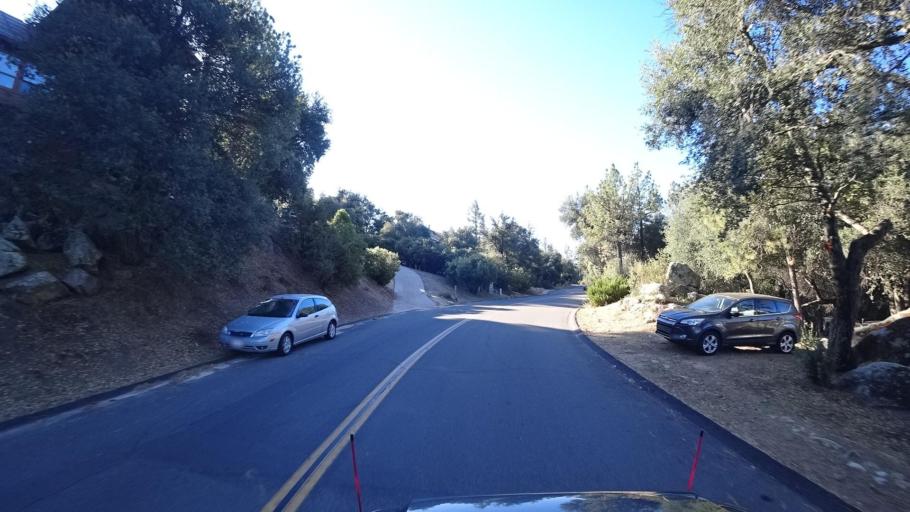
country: US
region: California
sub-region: San Diego County
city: Pine Valley
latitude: 32.8428
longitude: -116.5259
